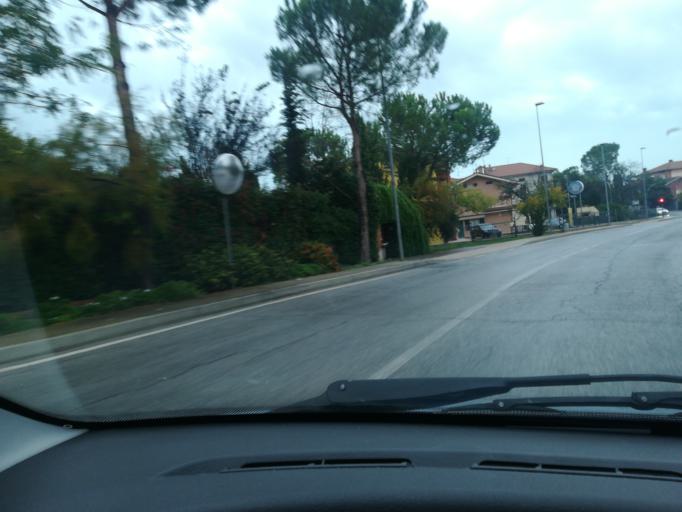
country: IT
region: The Marches
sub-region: Provincia di Macerata
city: Borgo Stazione
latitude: 43.2834
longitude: 13.6379
